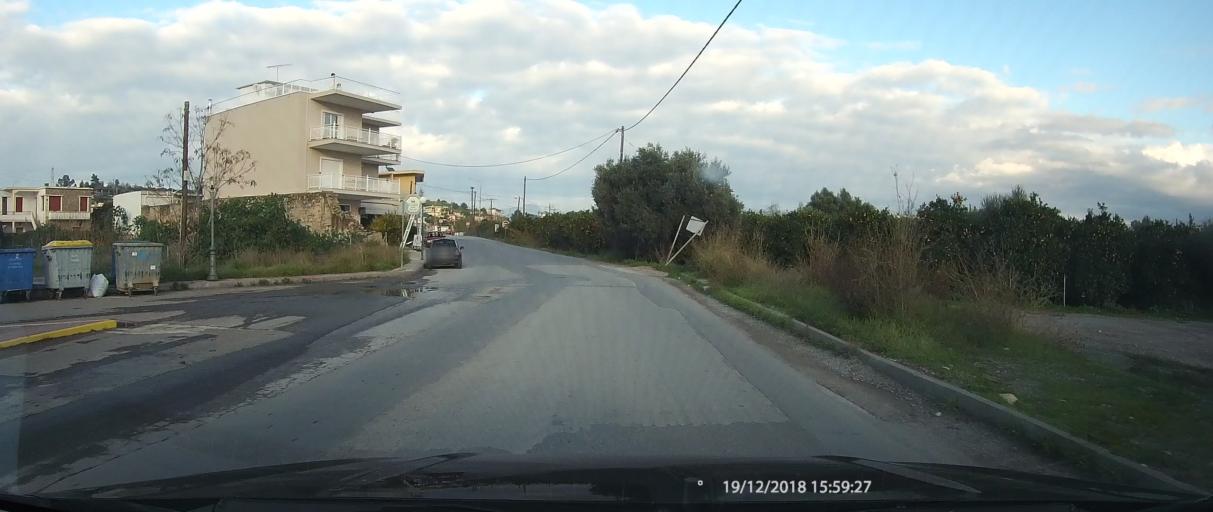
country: GR
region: Peloponnese
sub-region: Nomos Lakonias
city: Skala
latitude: 36.8524
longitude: 22.6730
